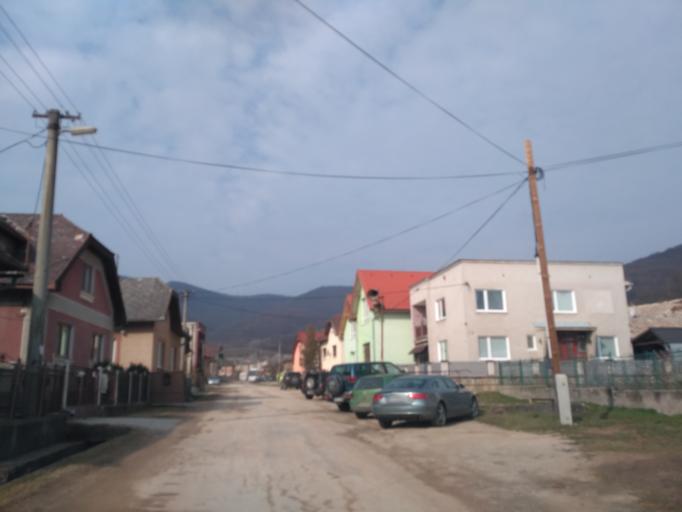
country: SK
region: Kosicky
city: Roznava
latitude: 48.6377
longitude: 20.4715
